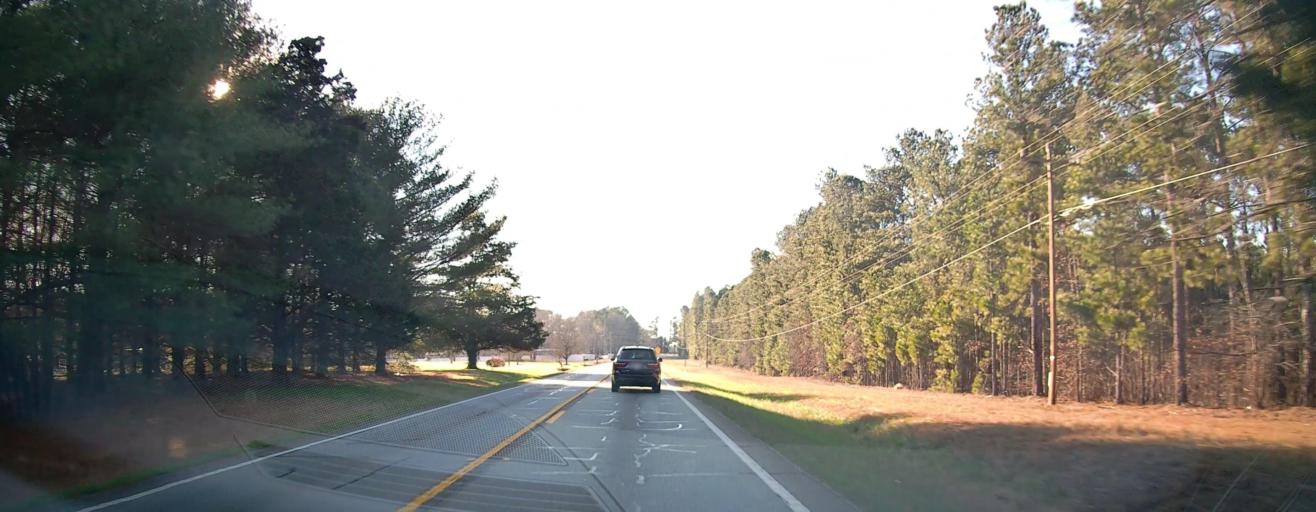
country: US
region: Georgia
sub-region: Henry County
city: Hampton
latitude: 33.4191
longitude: -84.2567
